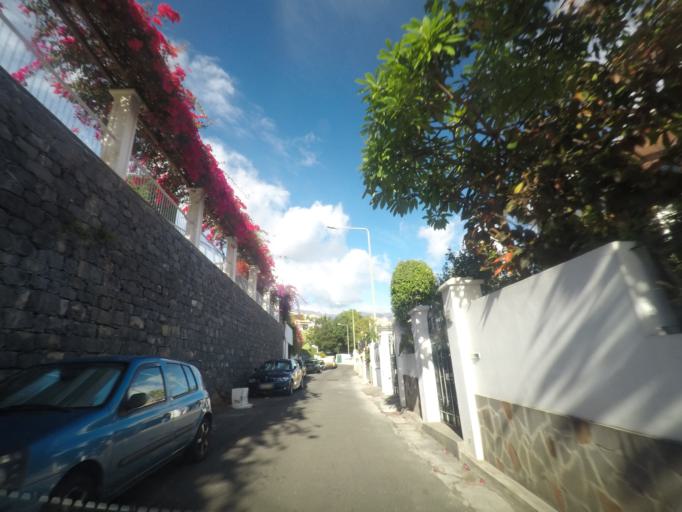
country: PT
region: Madeira
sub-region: Funchal
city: Funchal
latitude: 32.6414
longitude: -16.9306
